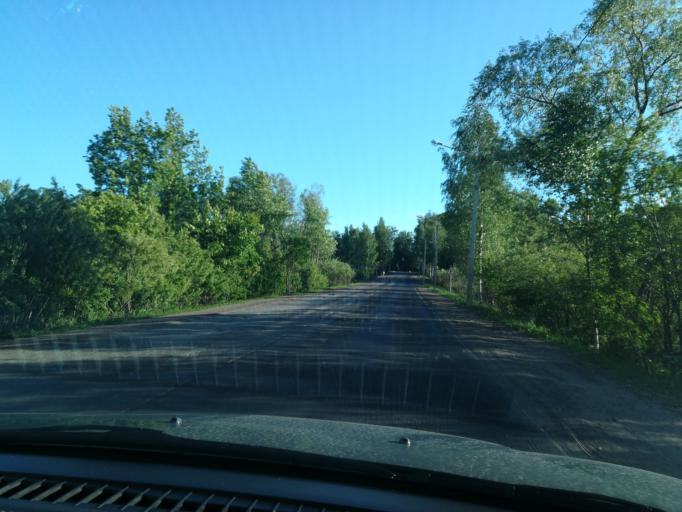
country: RU
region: Leningrad
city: Lesogorskiy
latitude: 61.0423
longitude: 28.9253
